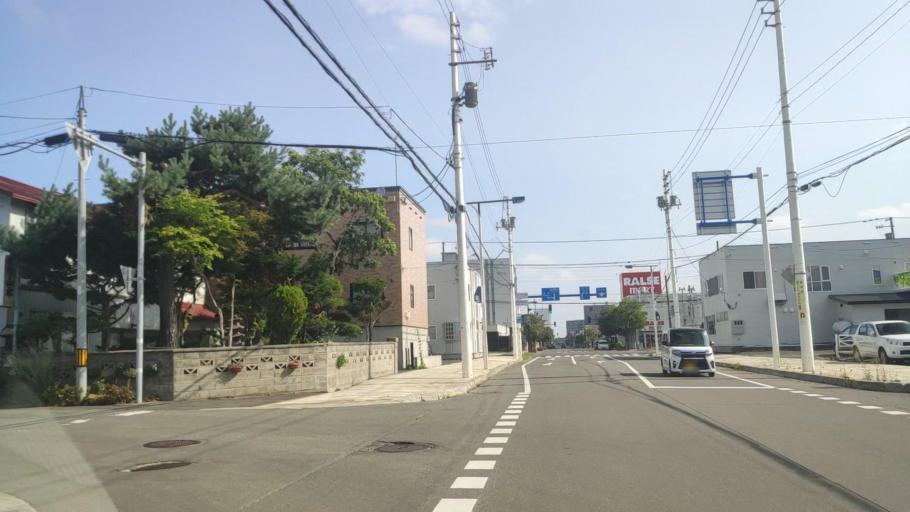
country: JP
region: Hokkaido
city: Shimo-furano
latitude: 43.3412
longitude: 142.3865
